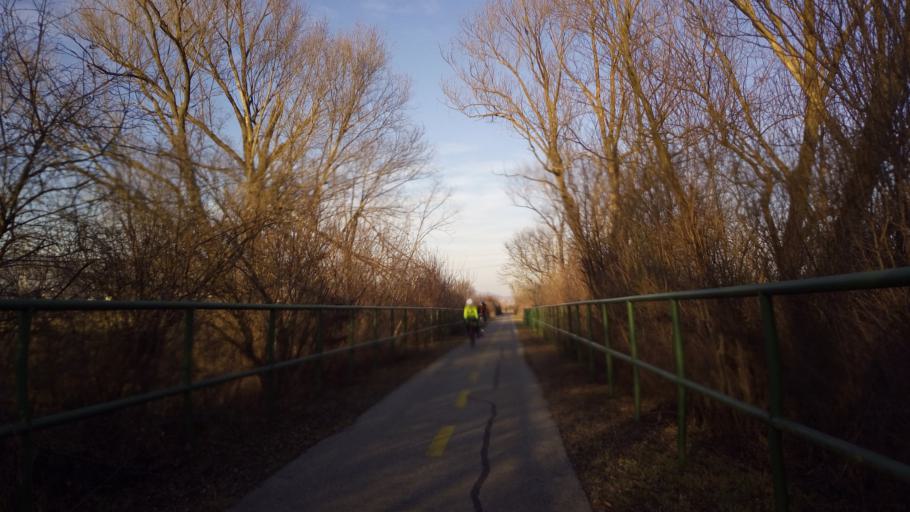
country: HU
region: Baranya
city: Pellerd
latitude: 46.0460
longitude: 18.1888
